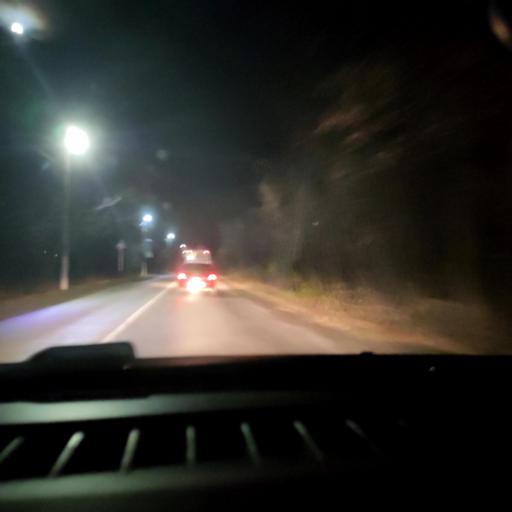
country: RU
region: Voronezj
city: Novaya Usman'
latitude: 51.6564
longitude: 39.3289
